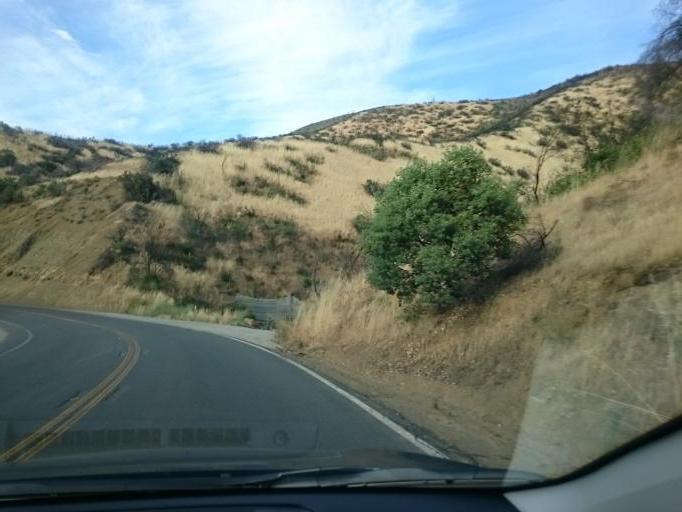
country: US
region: California
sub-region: Yolo County
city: Winters
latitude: 38.5054
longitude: -122.1116
